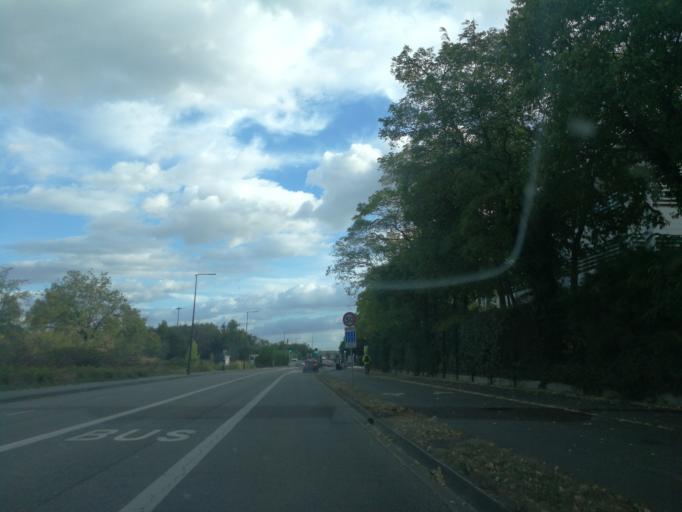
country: FR
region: Midi-Pyrenees
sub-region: Departement de la Haute-Garonne
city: Balma
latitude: 43.6302
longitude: 1.4759
